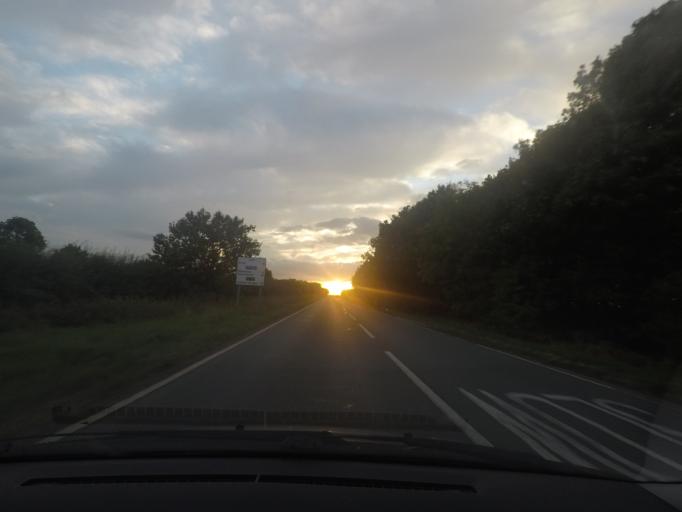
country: GB
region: England
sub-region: North Lincolnshire
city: Croxton
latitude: 53.5828
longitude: -0.3275
